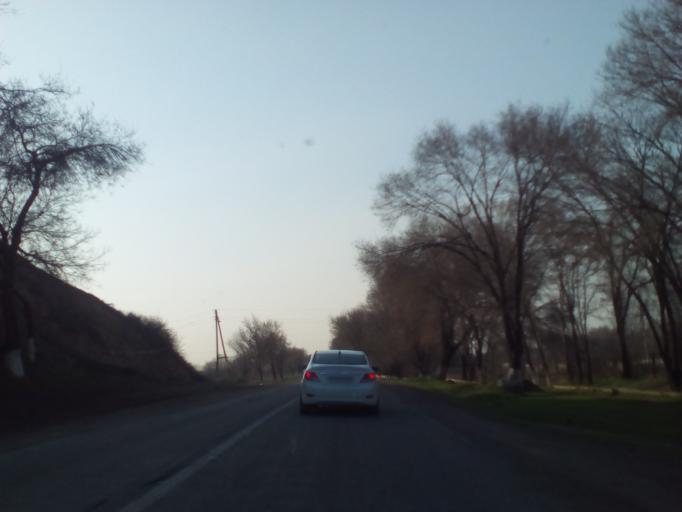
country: KZ
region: Almaty Oblysy
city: Burunday
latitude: 43.1716
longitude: 76.5314
